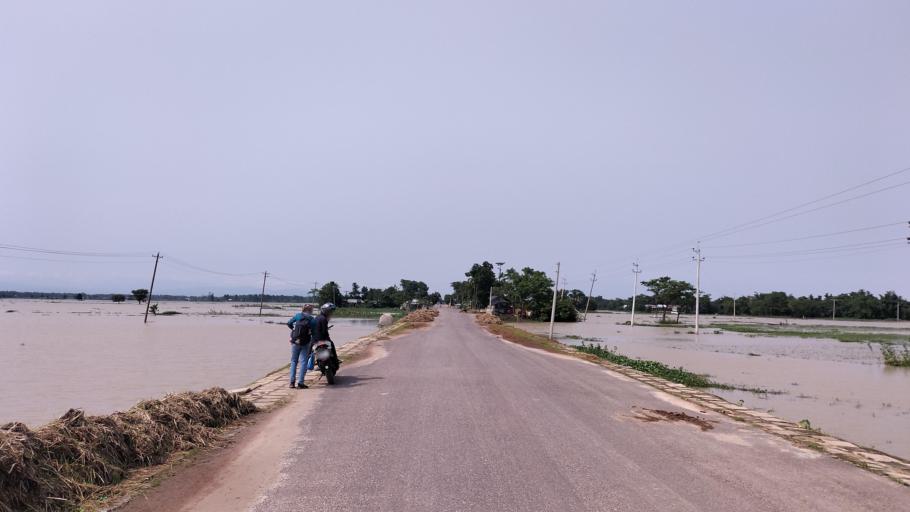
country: BD
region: Dhaka
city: Netrakona
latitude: 25.0136
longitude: 90.8537
